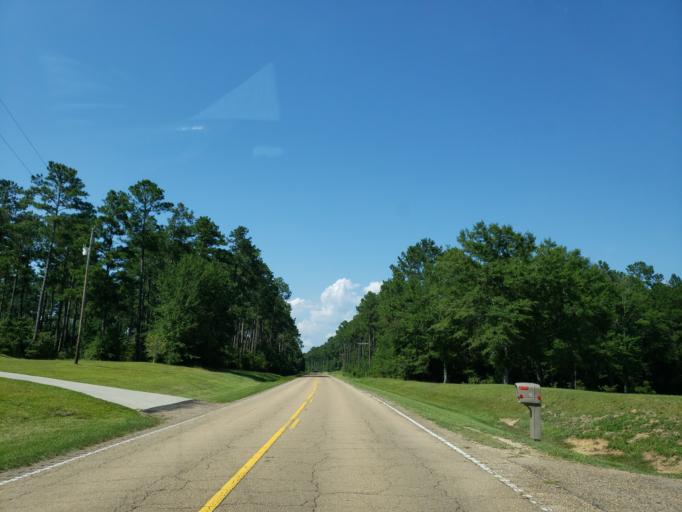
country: US
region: Mississippi
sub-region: Lamar County
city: Sumrall
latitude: 31.4405
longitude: -89.5317
